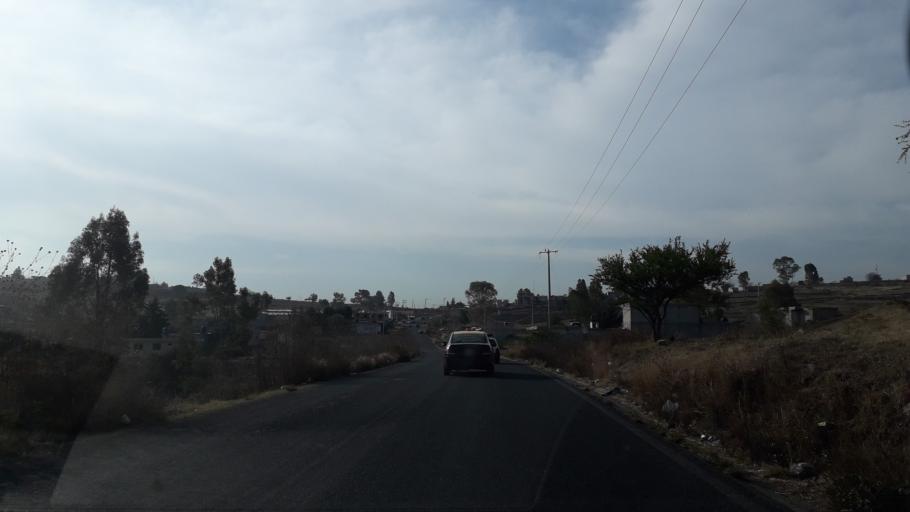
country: MX
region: Puebla
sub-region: Puebla
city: San Andres Azumiatla
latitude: 18.9155
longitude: -98.2453
